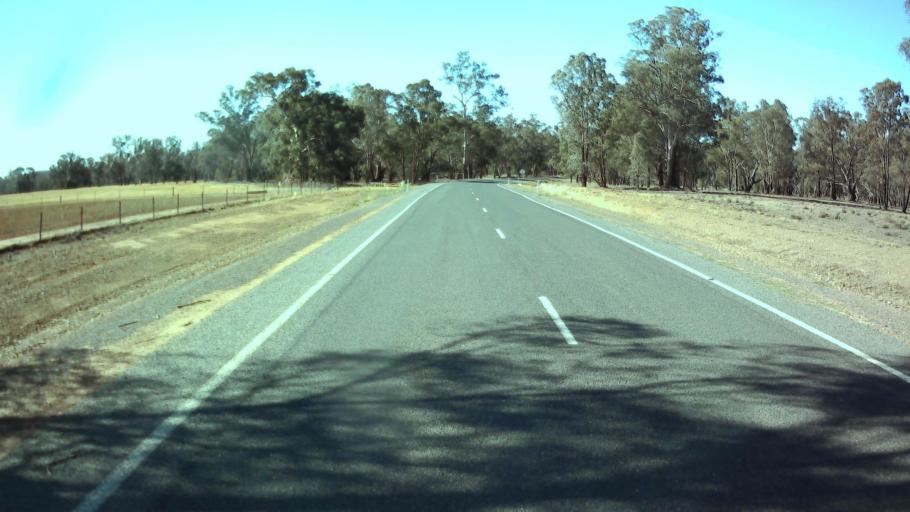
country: AU
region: New South Wales
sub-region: Weddin
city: Grenfell
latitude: -33.7651
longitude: 148.0822
